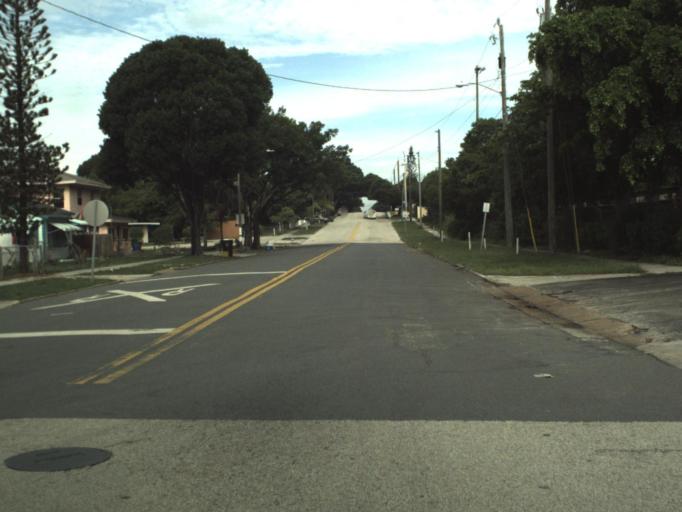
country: US
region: Florida
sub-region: Palm Beach County
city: West Palm Beach
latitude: 26.7273
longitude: -80.0572
